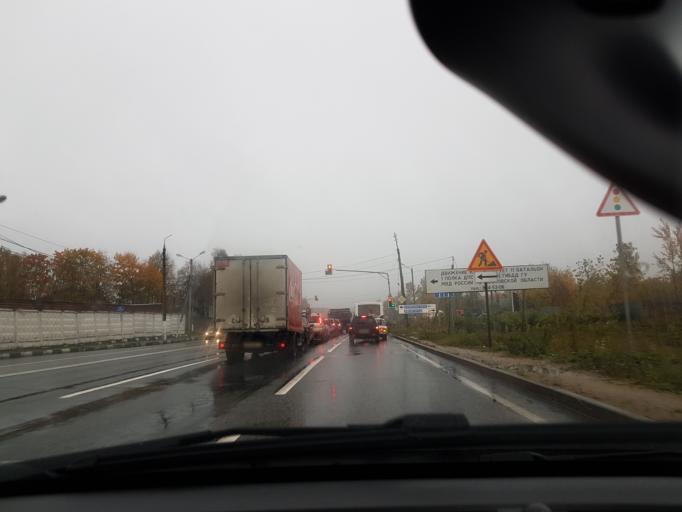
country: RU
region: Moskovskaya
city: Istra
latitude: 55.9043
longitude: 36.9436
